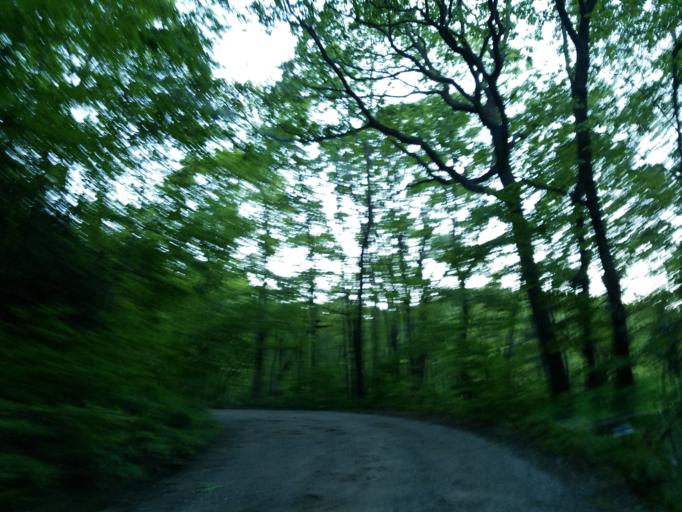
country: US
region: Georgia
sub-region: Lumpkin County
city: Dahlonega
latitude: 34.6661
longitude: -83.9789
